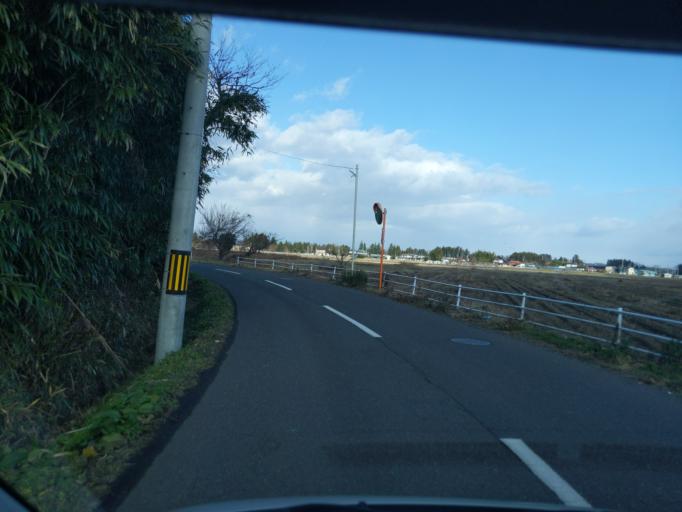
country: JP
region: Miyagi
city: Kogota
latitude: 38.7411
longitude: 141.0488
